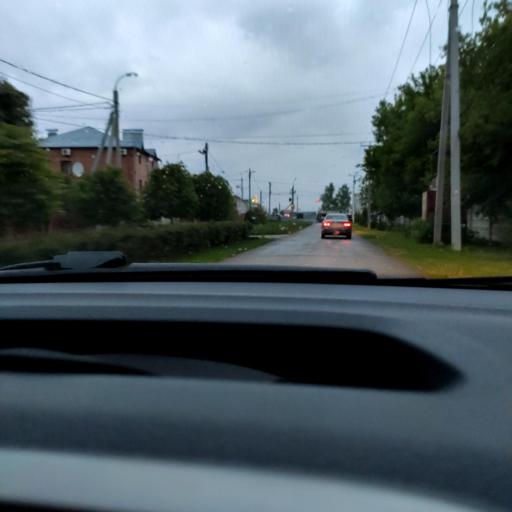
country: RU
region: Samara
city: Tol'yatti
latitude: 53.5428
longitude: 49.3798
